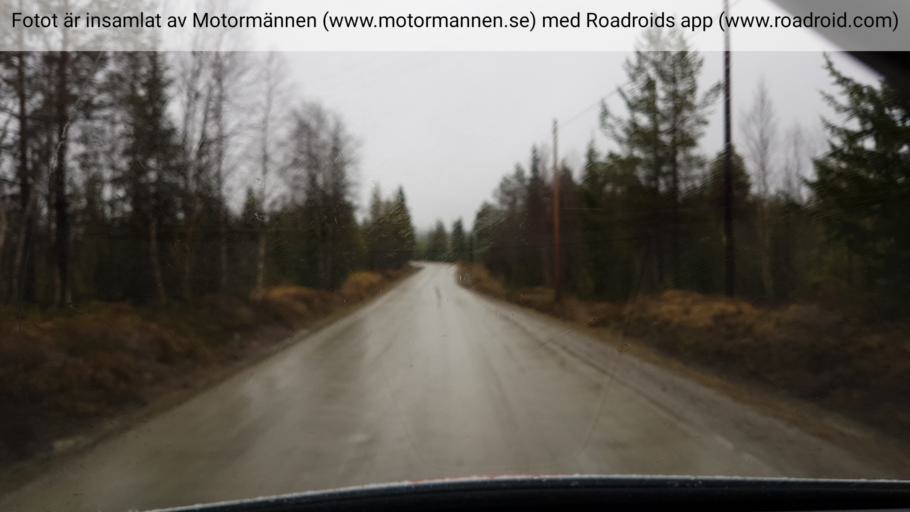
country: SE
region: Jaemtland
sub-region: Are Kommun
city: Jarpen
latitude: 62.5422
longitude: 13.4734
